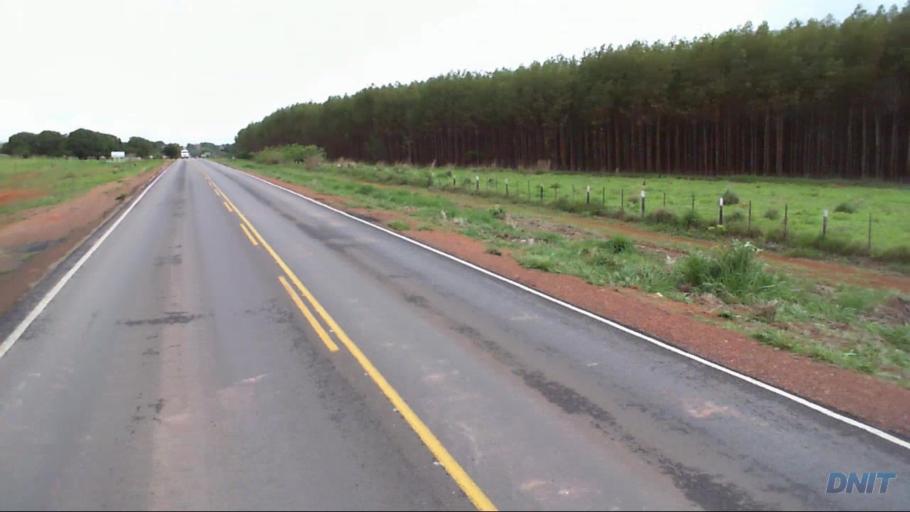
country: BR
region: Goias
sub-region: Padre Bernardo
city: Padre Bernardo
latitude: -15.2708
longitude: -48.2627
